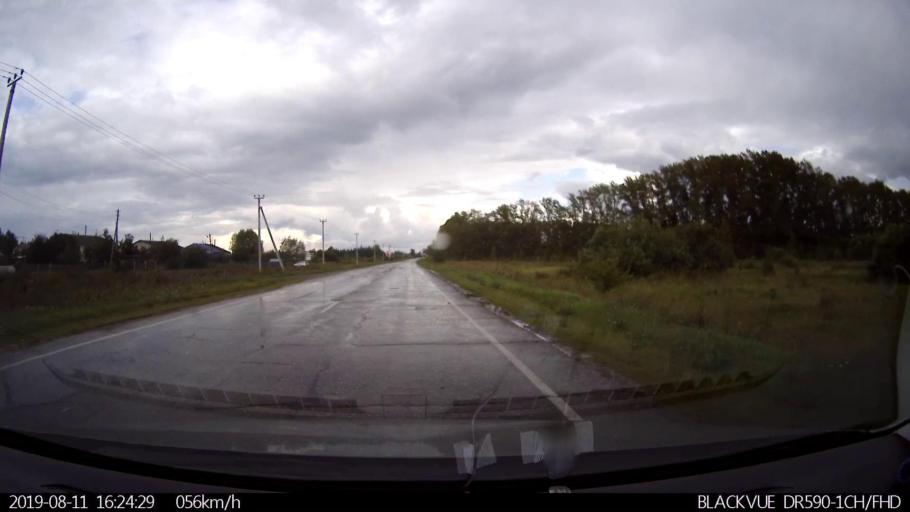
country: RU
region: Ulyanovsk
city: Mayna
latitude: 54.1007
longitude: 47.5949
